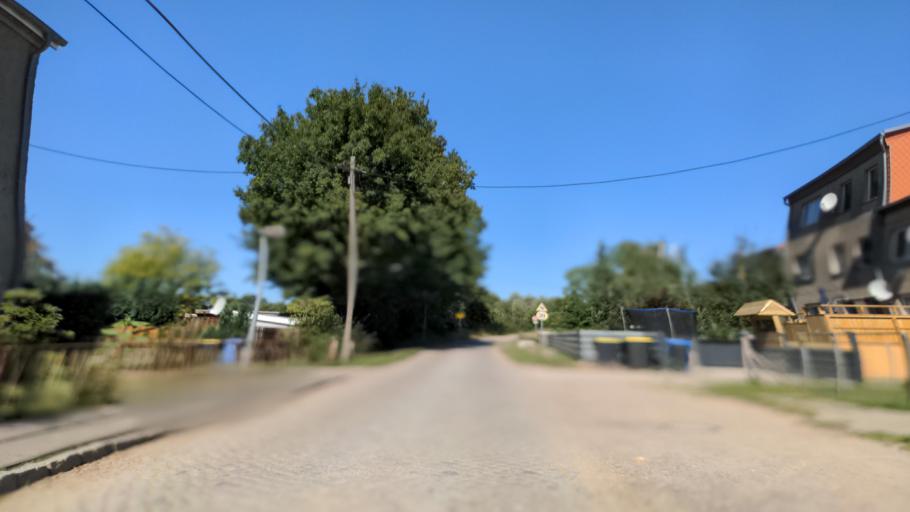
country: DE
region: Mecklenburg-Vorpommern
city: Selmsdorf
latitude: 53.8384
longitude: 10.8657
